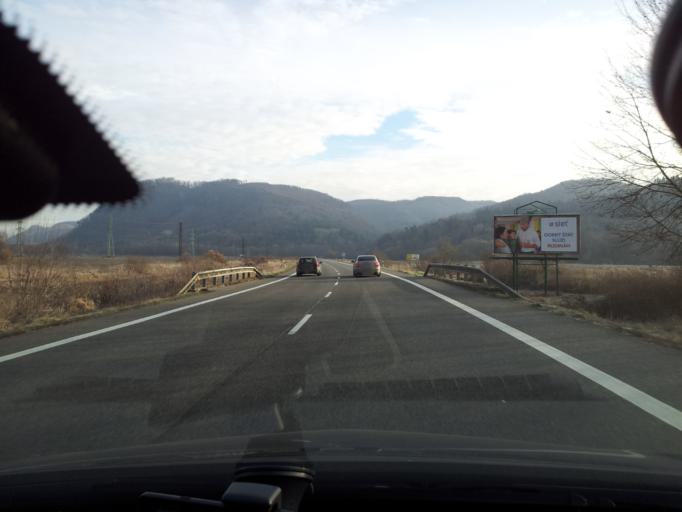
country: SK
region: Banskobystricky
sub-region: Okres Banska Bystrica
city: Banska Bystrica
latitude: 48.7461
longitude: 19.2398
